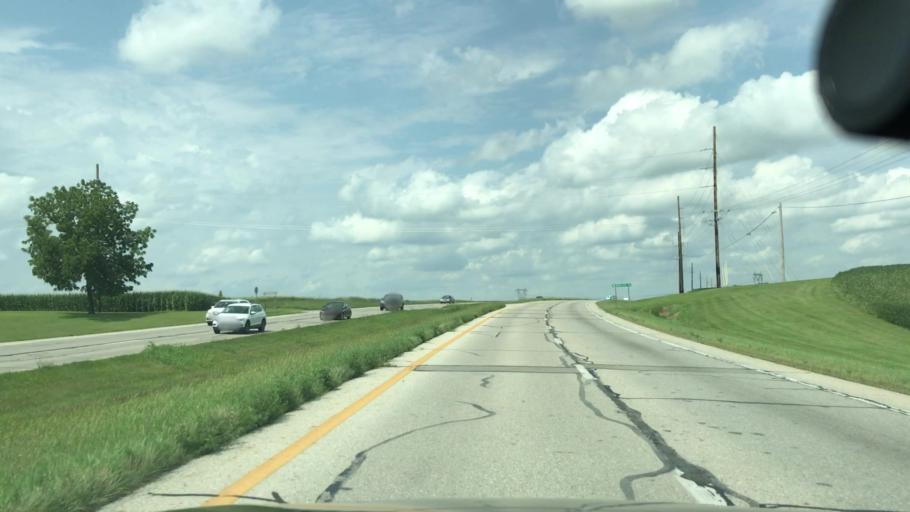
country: US
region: Ohio
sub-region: Pickaway County
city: Logan Elm Village
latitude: 39.5371
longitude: -82.9669
